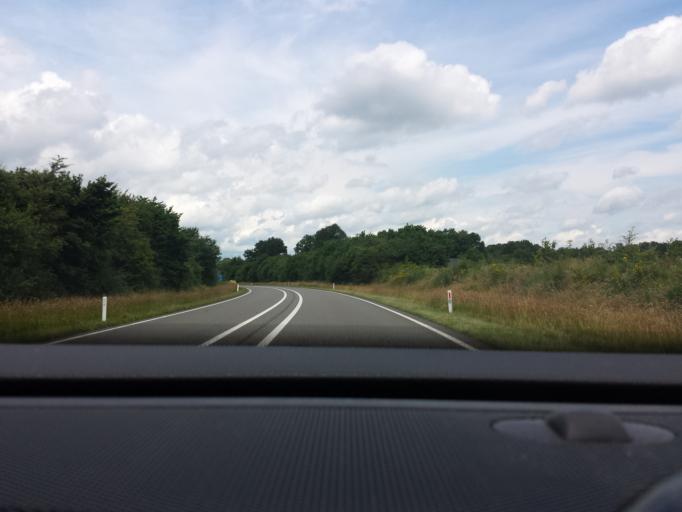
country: NL
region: Gelderland
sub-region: Gemeente Lochem
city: Barchem
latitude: 52.0849
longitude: 6.4651
